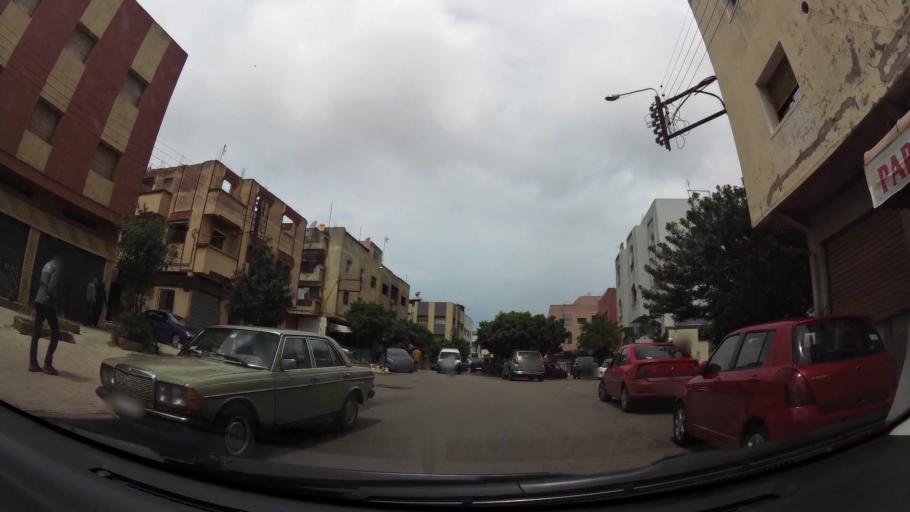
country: MA
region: Grand Casablanca
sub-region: Casablanca
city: Casablanca
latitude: 33.5521
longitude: -7.6834
